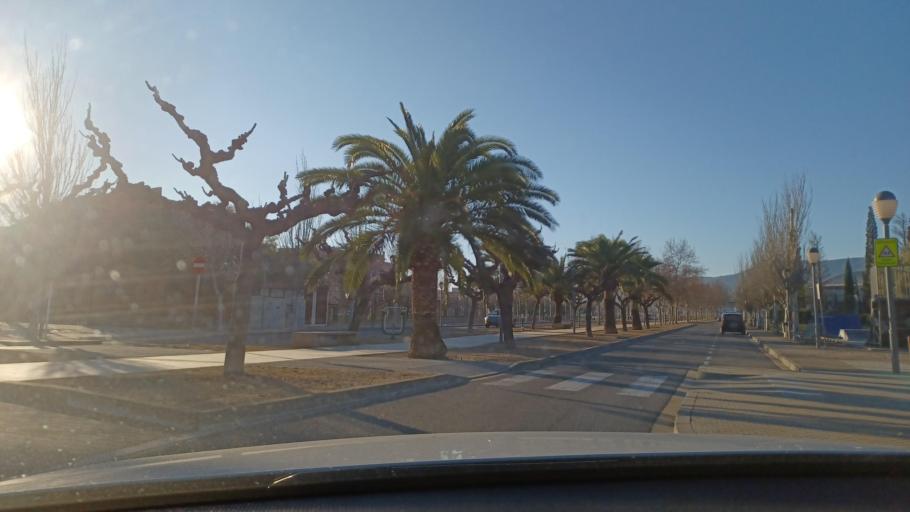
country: ES
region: Catalonia
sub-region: Provincia de Tarragona
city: Amposta
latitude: 40.7093
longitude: 0.5720
